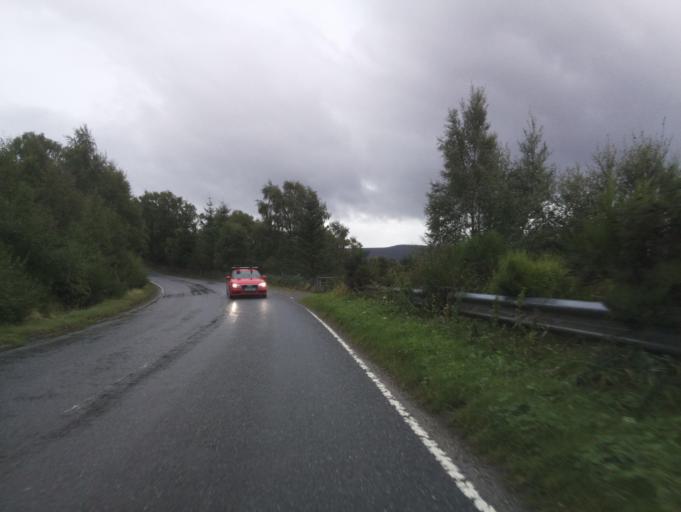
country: GB
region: Scotland
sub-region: Highland
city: Grantown on Spey
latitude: 57.2778
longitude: -3.5583
